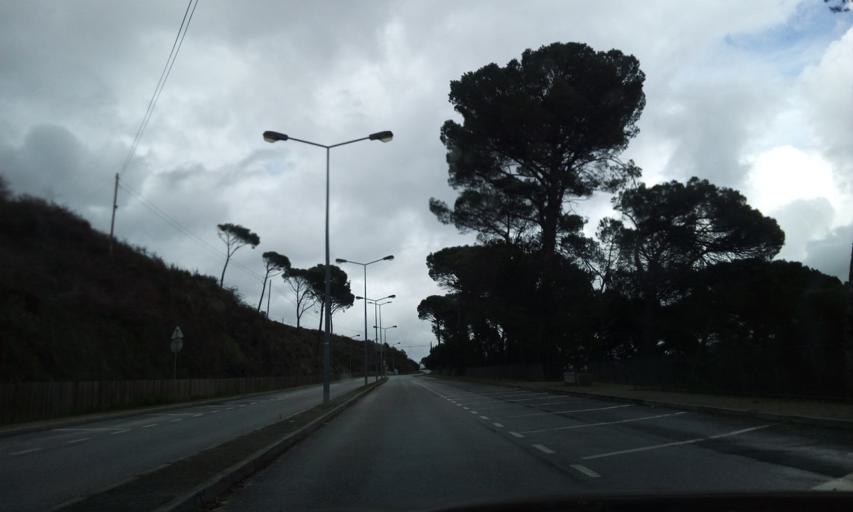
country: PT
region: Viseu
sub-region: Viseu
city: Rio de Loba
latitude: 40.6073
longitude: -7.8692
